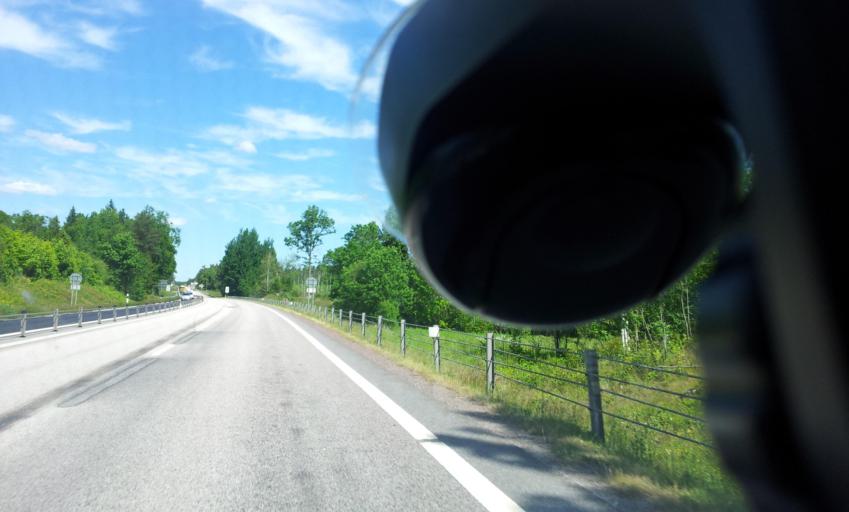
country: SE
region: Kalmar
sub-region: Oskarshamns Kommun
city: Oskarshamn
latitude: 57.3428
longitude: 16.4875
